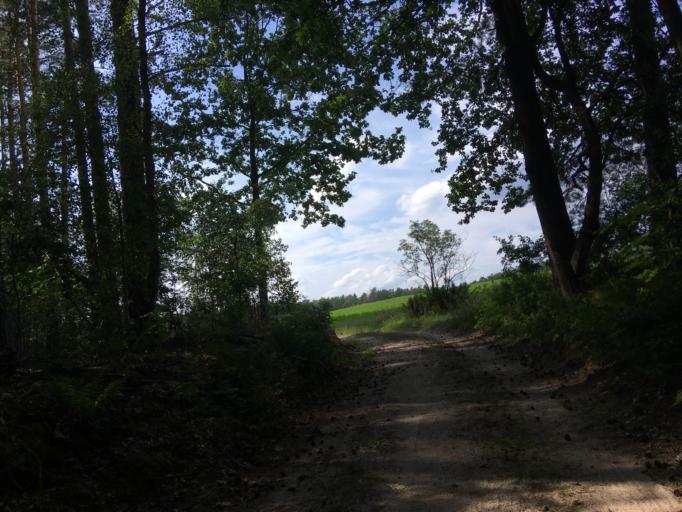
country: DE
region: Brandenburg
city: Rudnitz
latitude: 52.7464
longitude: 13.5809
